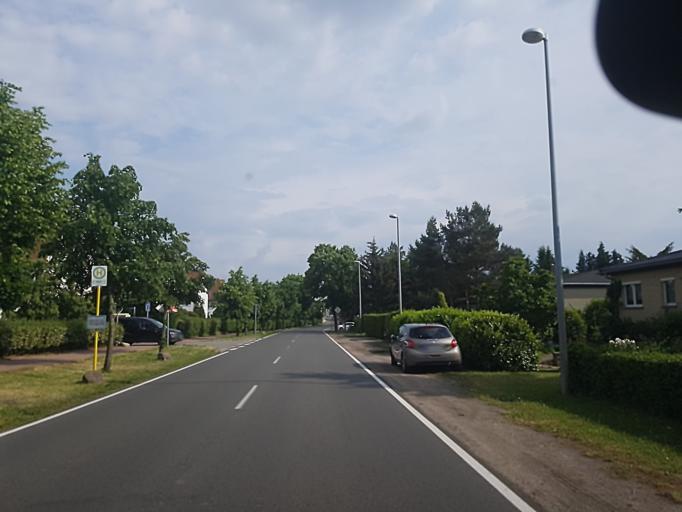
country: DE
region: Saxony-Anhalt
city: Coswig
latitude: 51.8922
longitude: 12.4493
